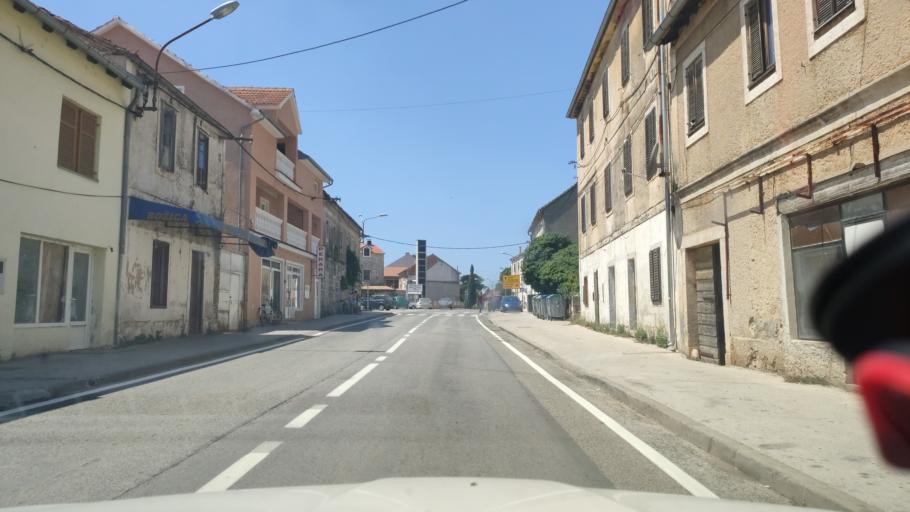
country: HR
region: Sibensko-Kniniska
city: Kistanje
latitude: 43.9807
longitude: 15.9621
